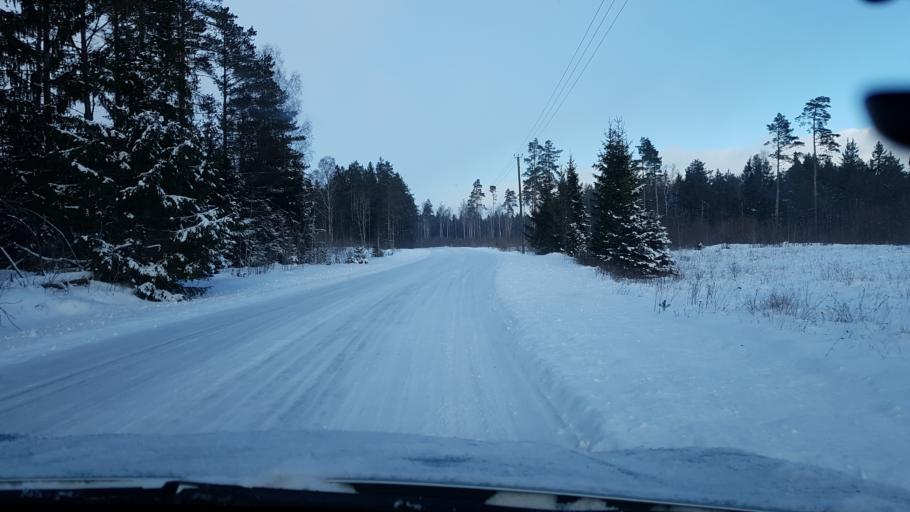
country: EE
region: Harju
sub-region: Nissi vald
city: Turba
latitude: 59.1915
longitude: 24.1397
